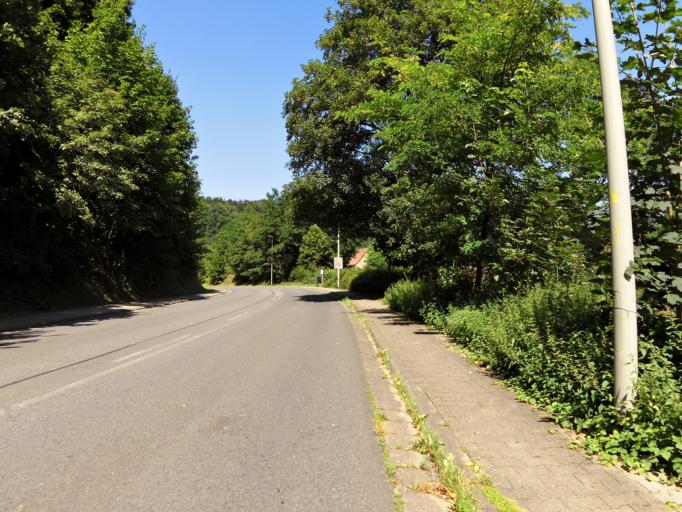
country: DE
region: Rheinland-Pfalz
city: Winnweiler
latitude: 49.5749
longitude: 7.8477
